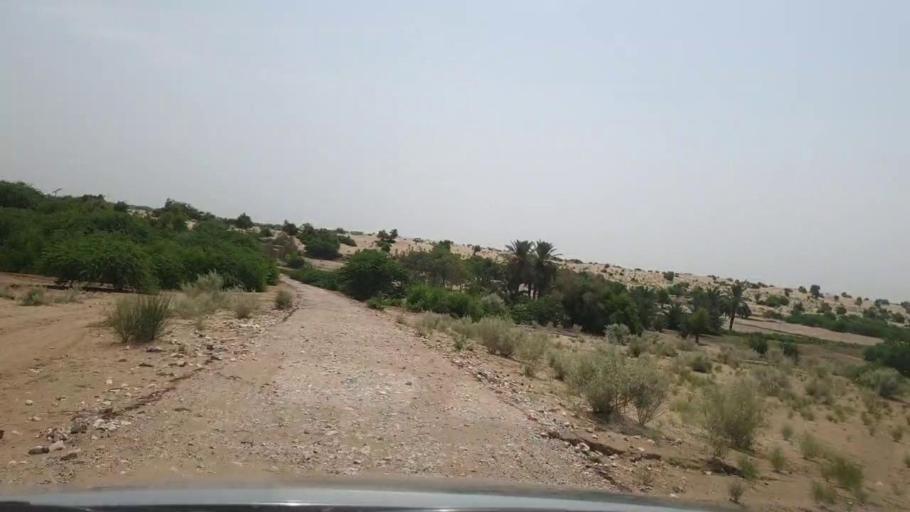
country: PK
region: Sindh
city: Pano Aqil
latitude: 27.5814
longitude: 69.1686
